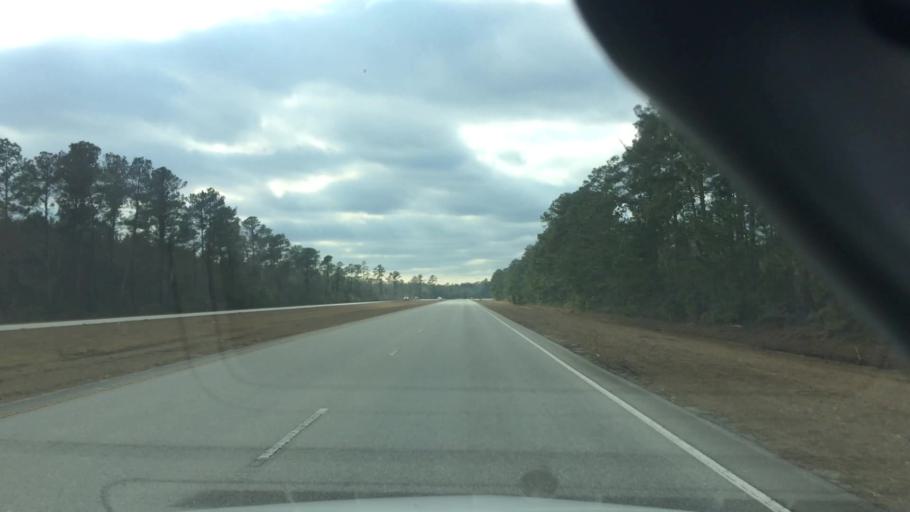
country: US
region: North Carolina
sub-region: Brunswick County
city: Bolivia
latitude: 34.0542
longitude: -78.2139
